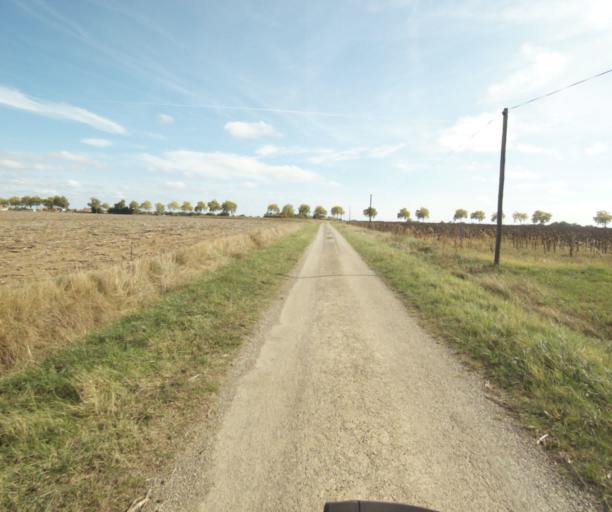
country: FR
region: Midi-Pyrenees
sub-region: Departement du Tarn-et-Garonne
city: Saint-Porquier
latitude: 43.9474
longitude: 1.1418
